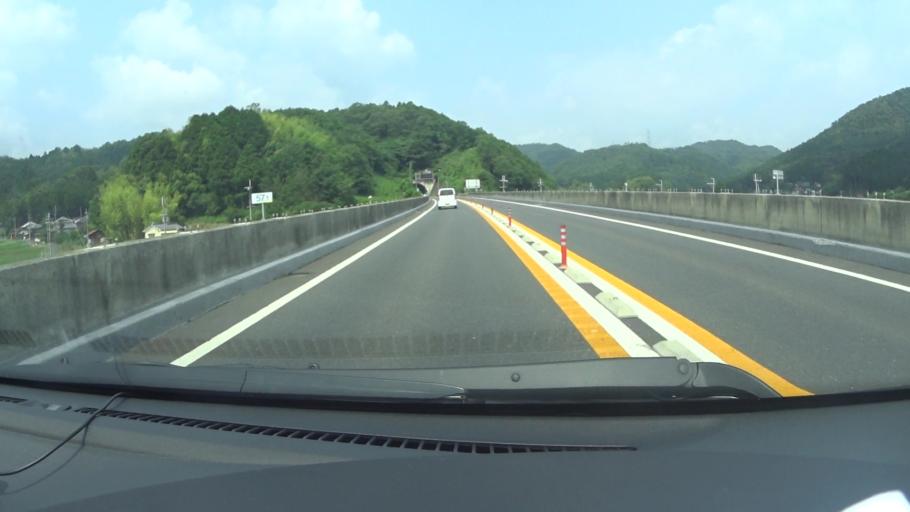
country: JP
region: Kyoto
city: Kameoka
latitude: 35.1273
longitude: 135.4724
